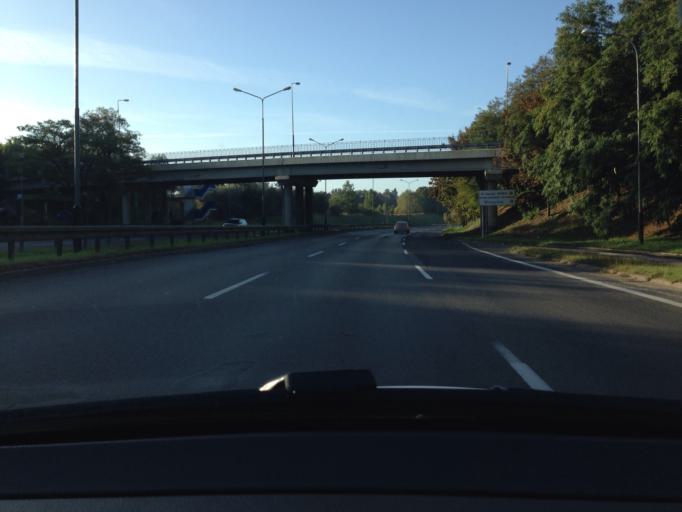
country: PL
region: Greater Poland Voivodeship
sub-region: Poznan
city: Poznan
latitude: 52.4405
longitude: 16.9097
